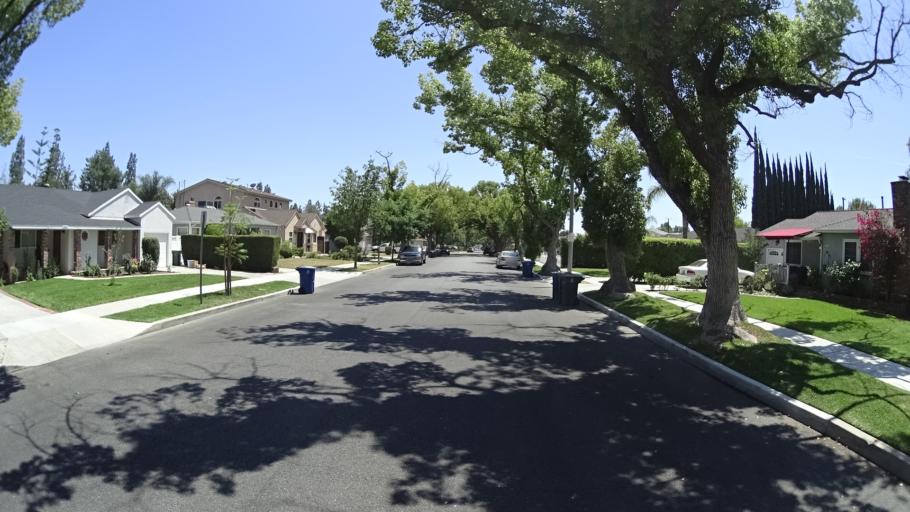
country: US
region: California
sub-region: Los Angeles County
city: Burbank
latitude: 34.1822
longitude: -118.3437
